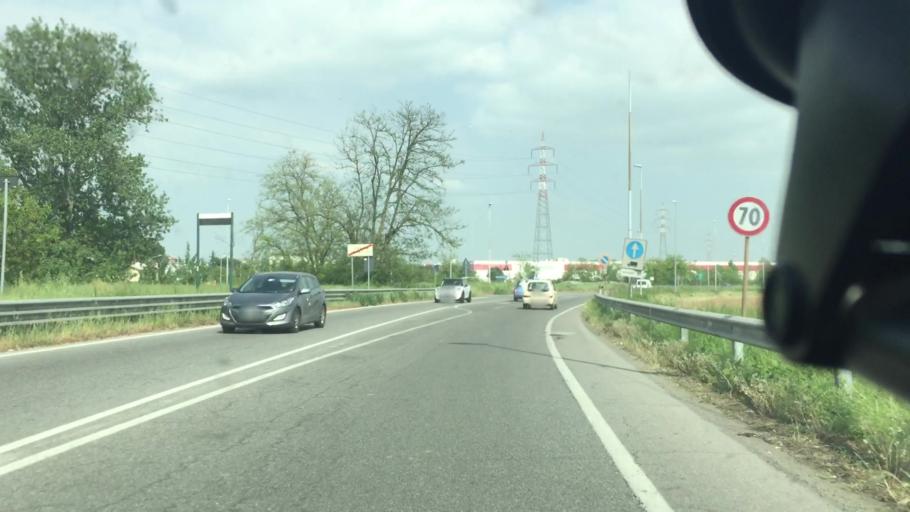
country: IT
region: Lombardy
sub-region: Citta metropolitana di Milano
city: Sant'Agata Martesana
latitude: 45.5247
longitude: 9.3893
